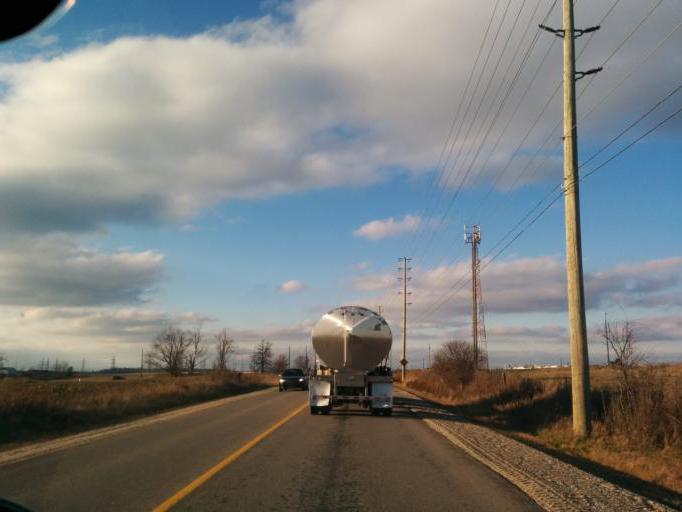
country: CA
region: Ontario
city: Oakville
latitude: 43.5206
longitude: -79.7140
